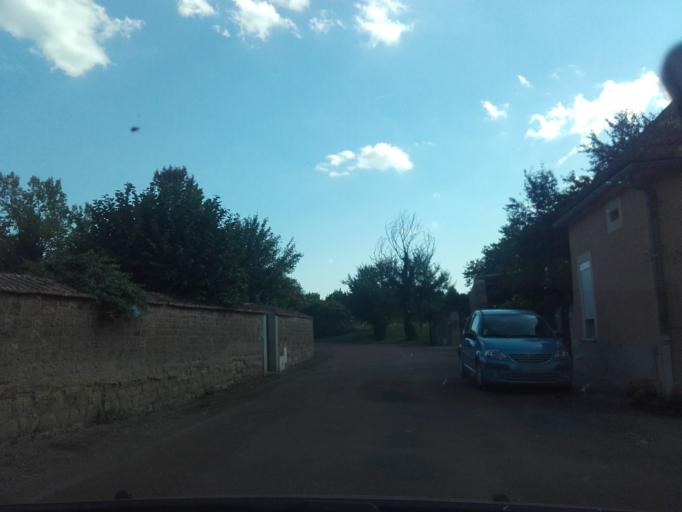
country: FR
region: Bourgogne
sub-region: Departement de Saone-et-Loire
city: Epinac
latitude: 47.0083
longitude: 4.4733
